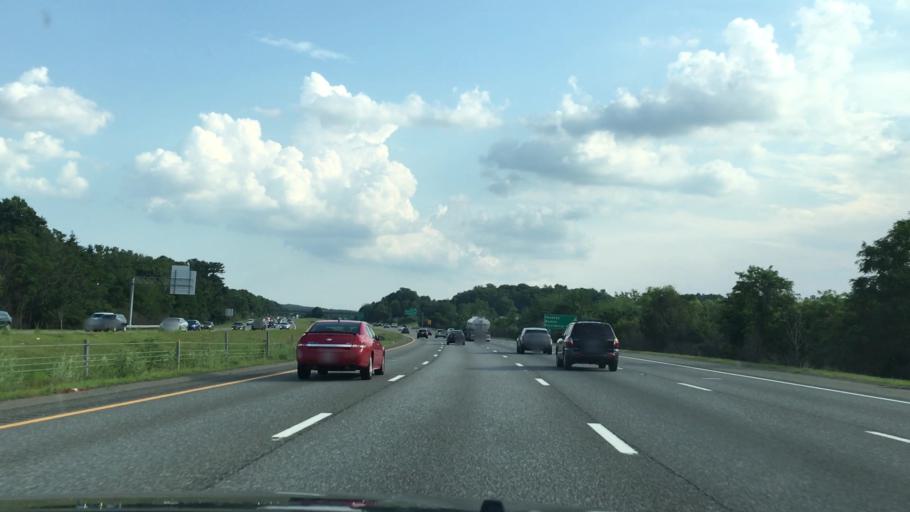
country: US
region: Massachusetts
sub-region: Essex County
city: Danvers
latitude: 42.5754
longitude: -70.9694
